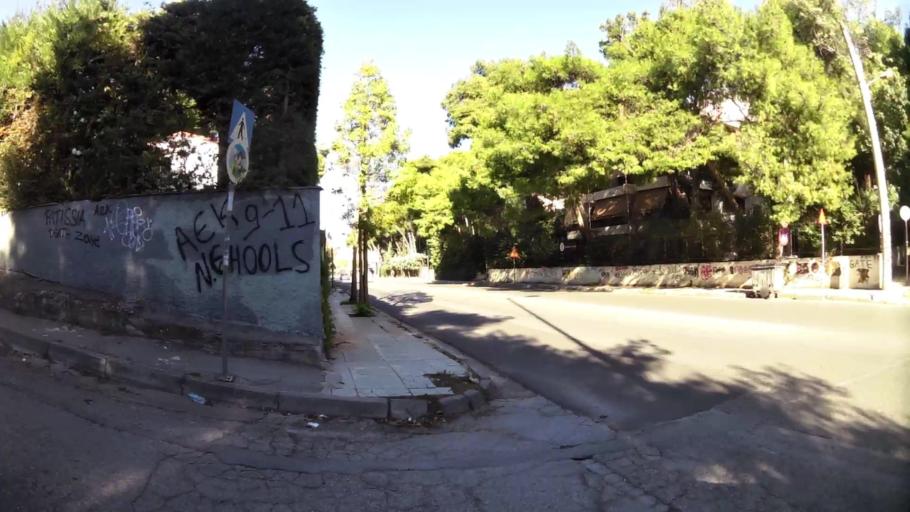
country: GR
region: Attica
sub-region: Nomarchia Athinas
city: Nea Erythraia
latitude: 38.0935
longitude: 23.8227
